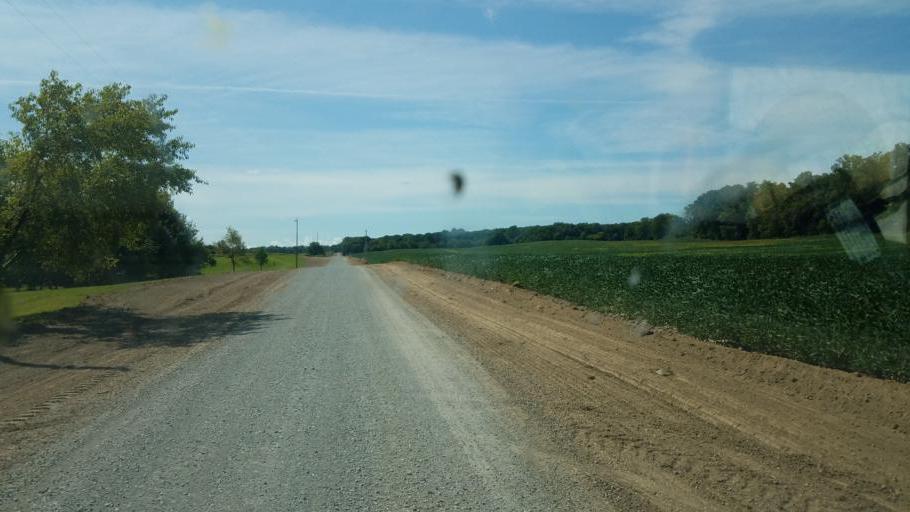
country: US
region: Ohio
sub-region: Knox County
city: Centerburg
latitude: 40.4407
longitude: -82.7175
